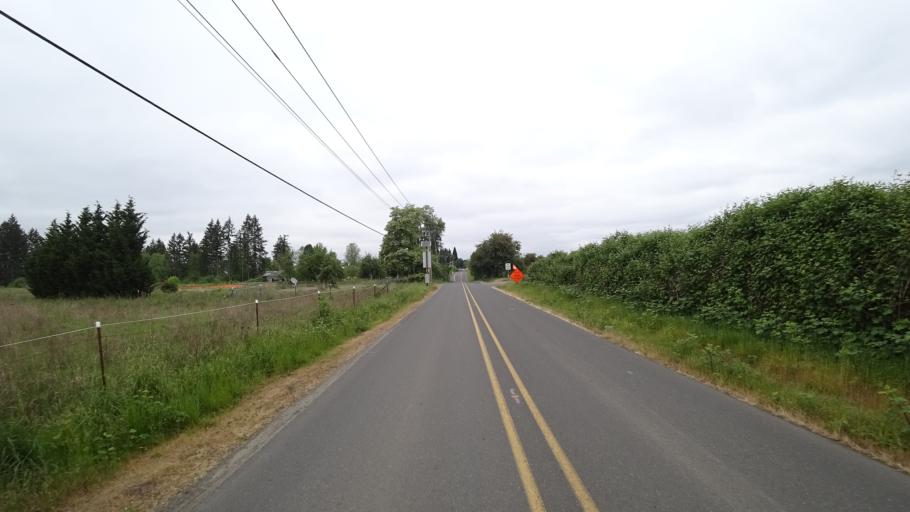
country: US
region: Oregon
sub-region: Washington County
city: Aloha
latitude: 45.4926
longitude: -122.9125
